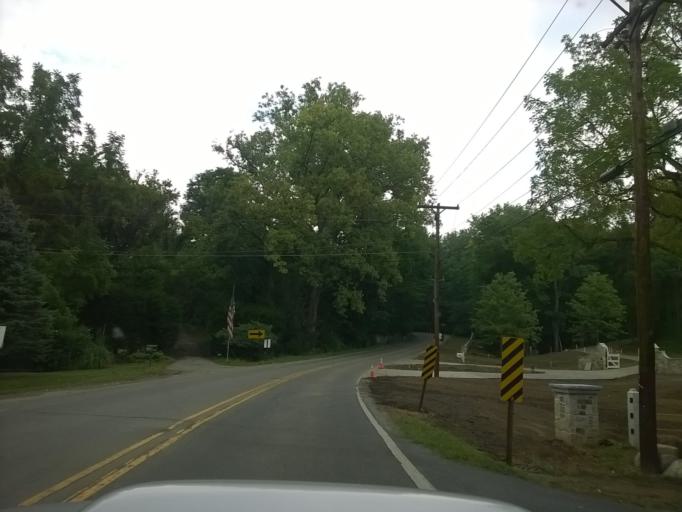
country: US
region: Indiana
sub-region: Marion County
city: Meridian Hills
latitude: 39.9010
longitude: -86.1650
